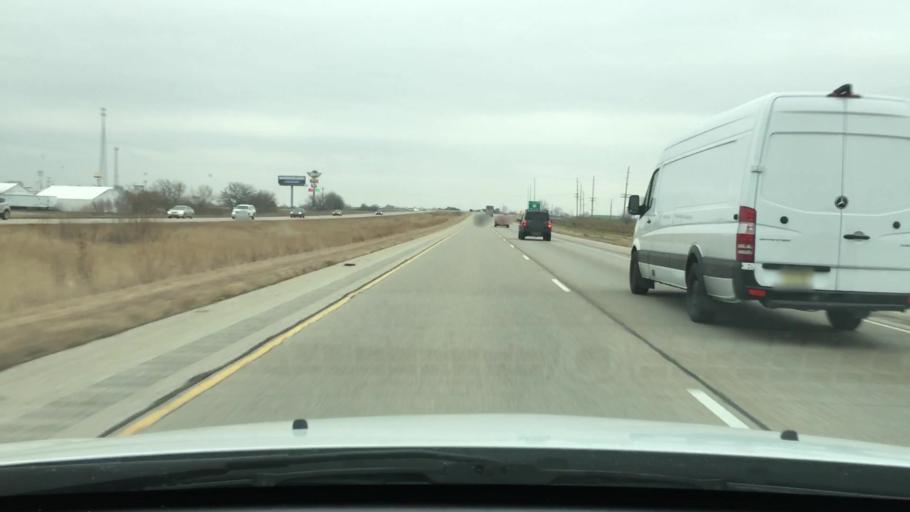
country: US
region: Illinois
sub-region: Logan County
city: Atlanta
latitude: 40.3067
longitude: -89.1725
